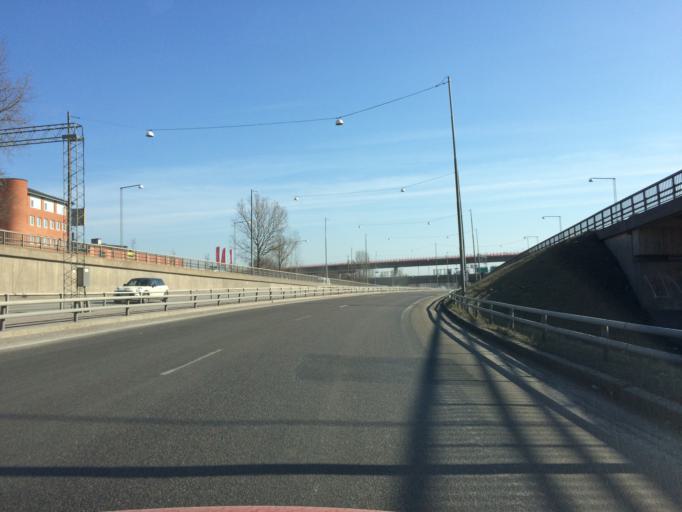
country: SE
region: Stockholm
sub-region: Stockholms Kommun
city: Arsta
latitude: 59.3008
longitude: 18.0235
